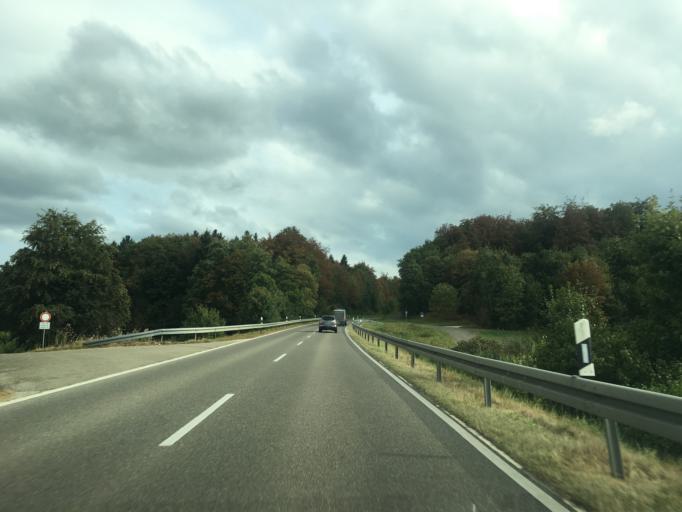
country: DE
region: Baden-Wuerttemberg
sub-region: Tuebingen Region
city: Gomadingen
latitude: 48.3733
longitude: 9.3176
